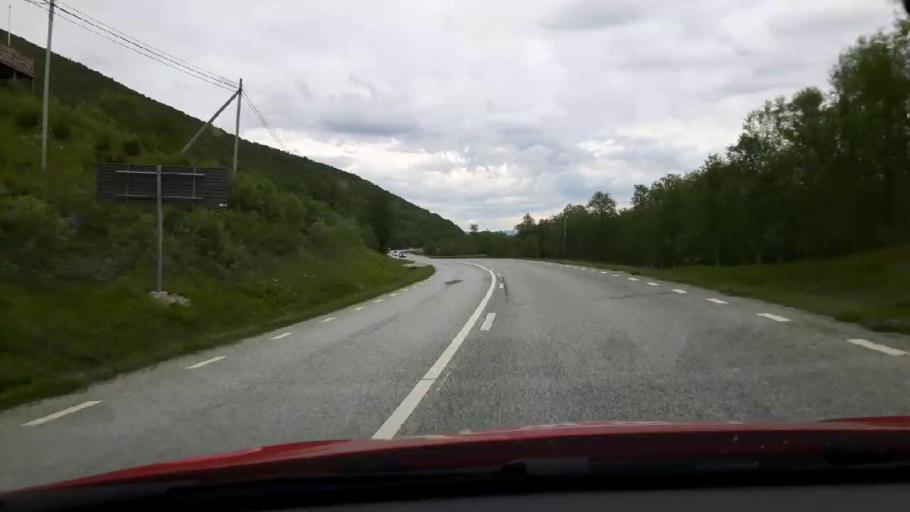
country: NO
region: Sor-Trondelag
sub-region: Tydal
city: Aas
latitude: 62.5608
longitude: 12.2592
